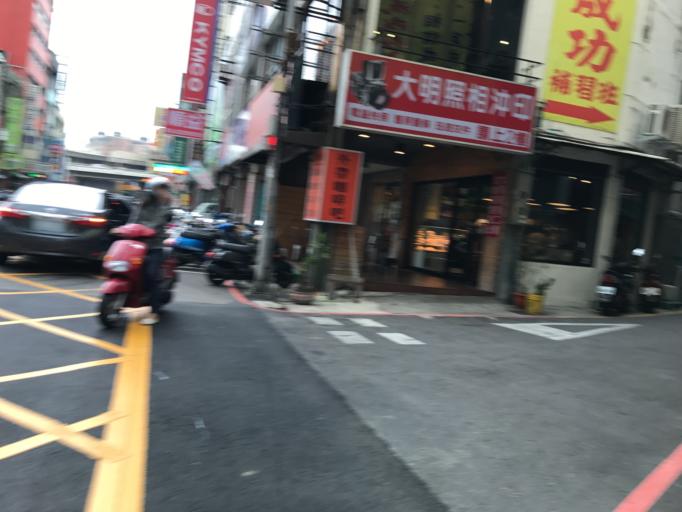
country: TW
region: Taiwan
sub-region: Hsinchu
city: Hsinchu
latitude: 24.8041
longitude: 120.9735
